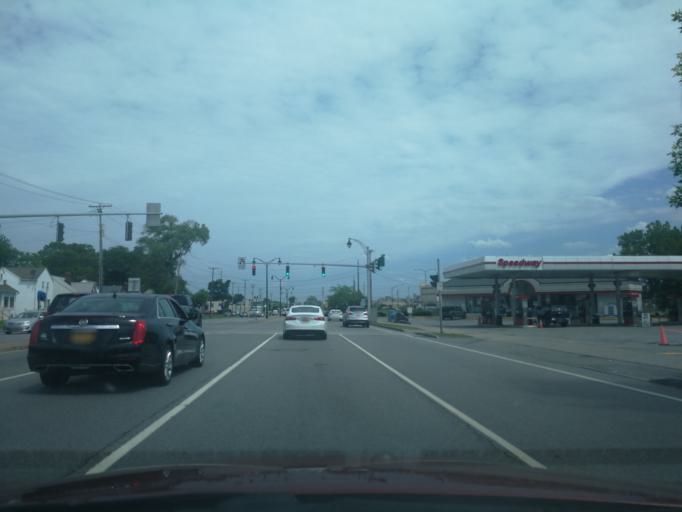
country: US
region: New York
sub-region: Monroe County
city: Greece
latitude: 43.2033
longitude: -77.6525
